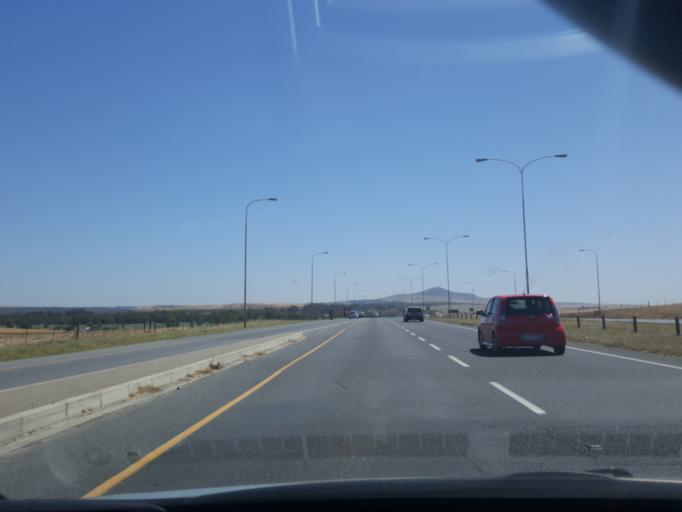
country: ZA
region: Western Cape
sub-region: City of Cape Town
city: Sunset Beach
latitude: -33.8048
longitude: 18.5476
